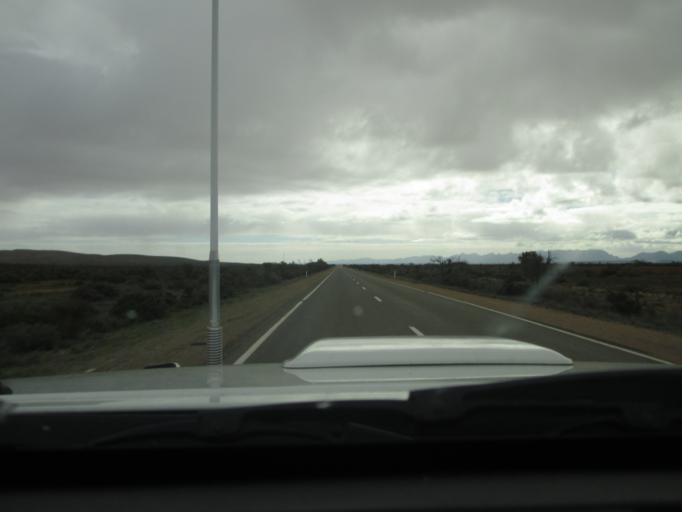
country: AU
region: South Australia
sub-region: Flinders Ranges
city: Quorn
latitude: -31.5162
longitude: 138.4276
